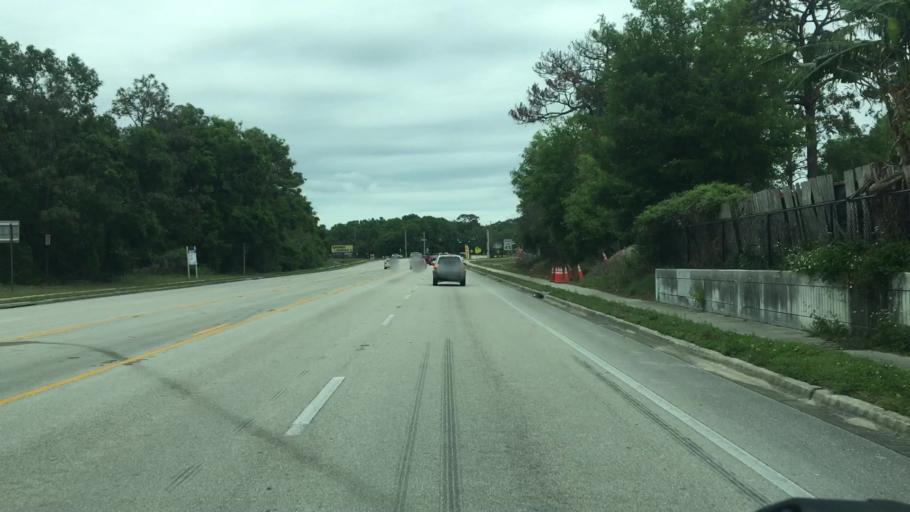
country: US
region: Florida
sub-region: Volusia County
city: De Land Southwest
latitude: 29.0111
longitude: -81.3216
